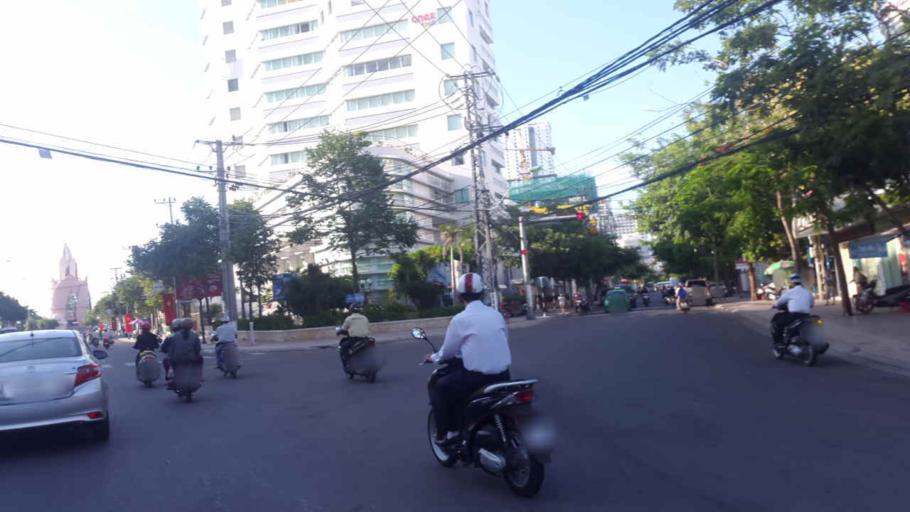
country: VN
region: Khanh Hoa
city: Nha Trang
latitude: 12.2424
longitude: 109.1946
